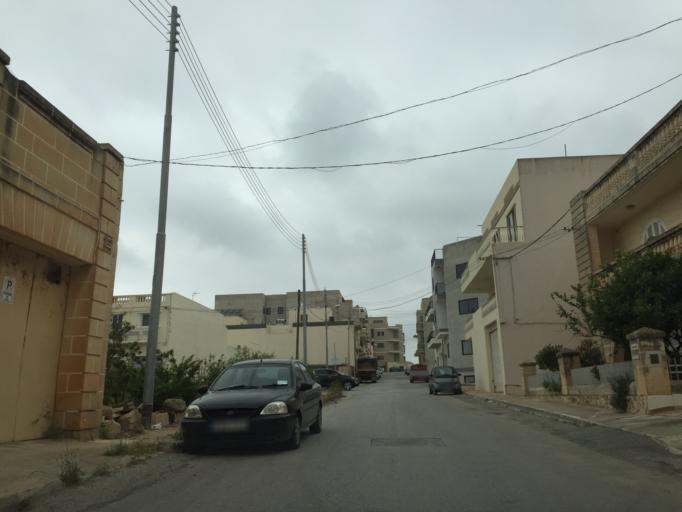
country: MT
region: L-Imgarr
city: Imgarr
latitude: 35.9212
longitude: 14.3684
